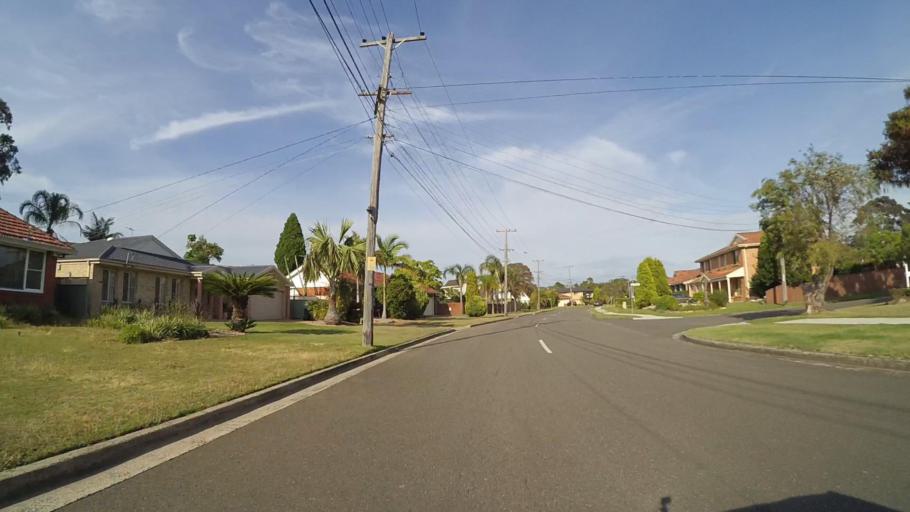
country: AU
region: New South Wales
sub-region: Kogarah
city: Blakehurst
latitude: -34.0142
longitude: 151.1102
